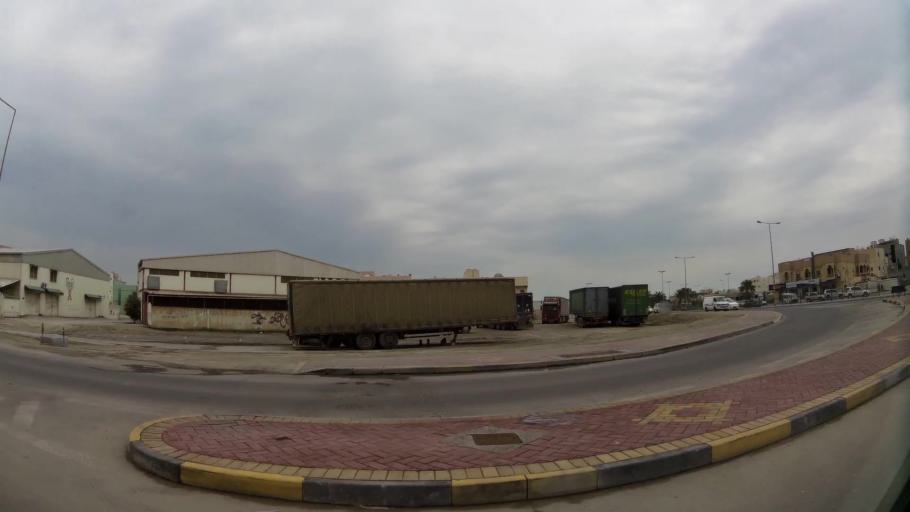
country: BH
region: Northern
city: Sitrah
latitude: 26.1657
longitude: 50.6128
